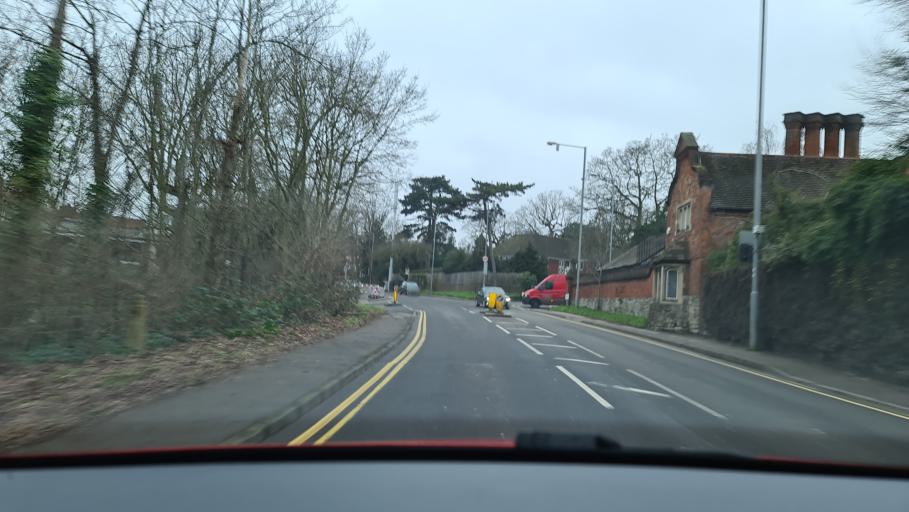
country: GB
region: England
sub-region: Greater London
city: New Malden
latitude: 51.4166
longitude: -0.2606
